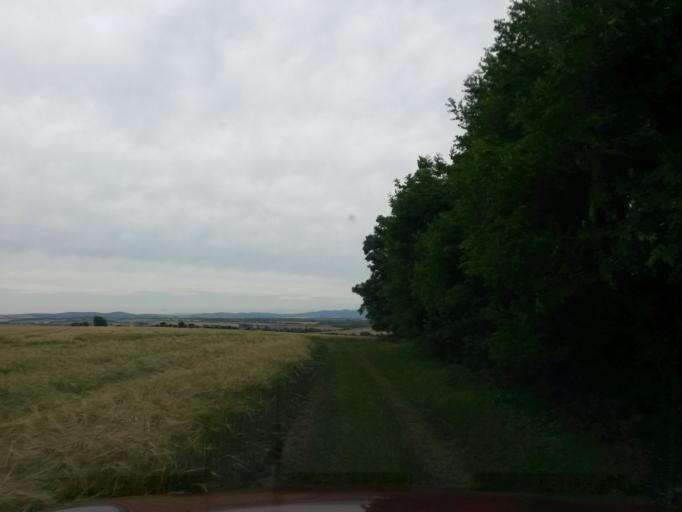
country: SK
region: Nitriansky
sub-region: Okres Nitra
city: Nitra
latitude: 48.3514
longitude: 17.9823
